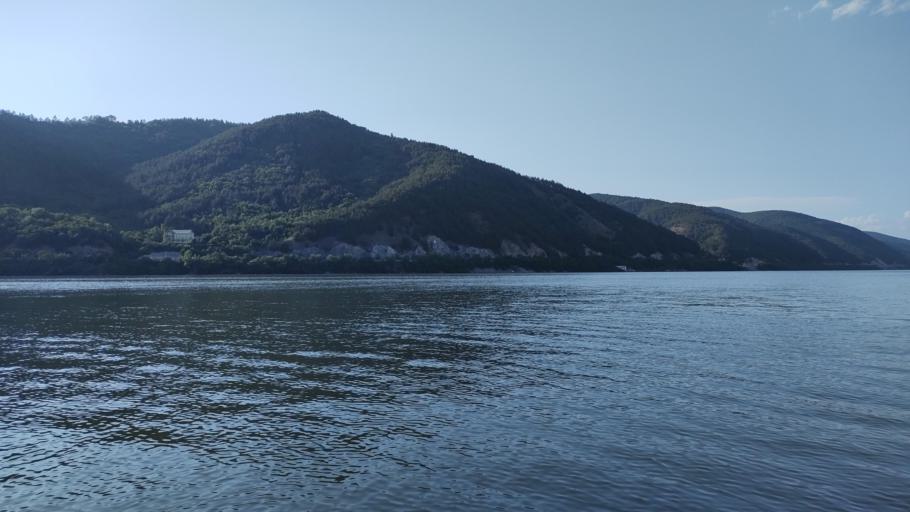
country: RO
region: Mehedinti
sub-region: Comuna Svinita
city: Svinita
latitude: 44.5165
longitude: 22.2020
